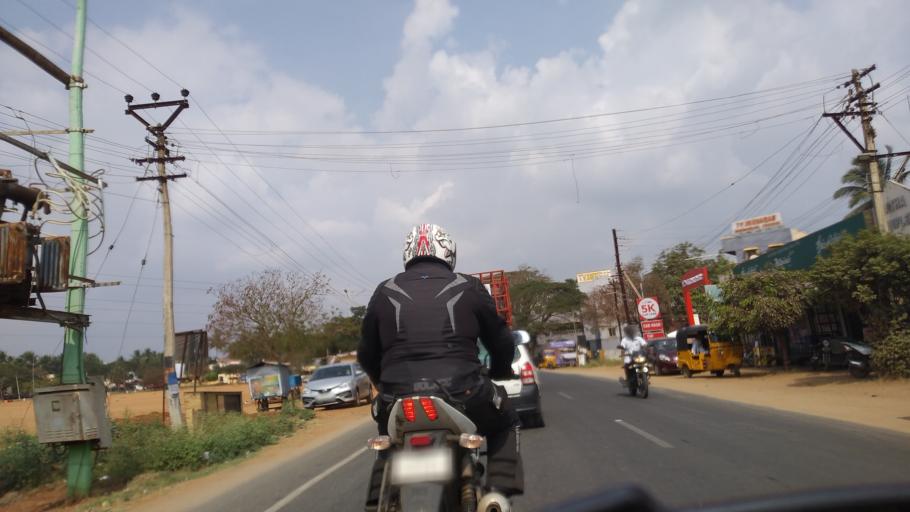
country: IN
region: Tamil Nadu
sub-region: Coimbatore
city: Perur
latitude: 10.9460
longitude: 76.9374
